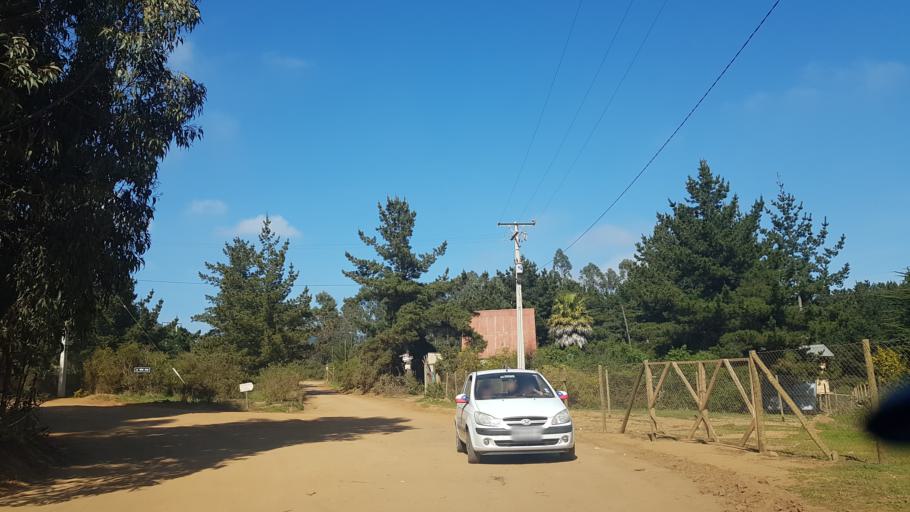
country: CL
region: Valparaiso
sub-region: Provincia de Valparaiso
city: Valparaiso
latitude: -33.1291
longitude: -71.6673
